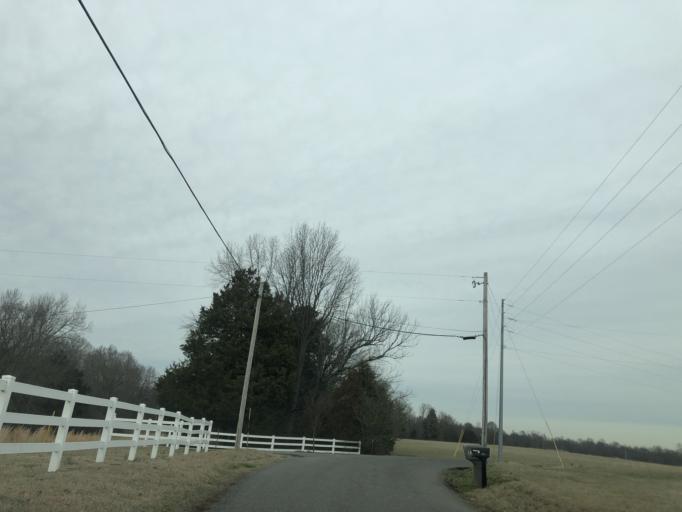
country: US
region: Tennessee
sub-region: Robertson County
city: Greenbrier
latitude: 36.4503
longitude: -86.7940
